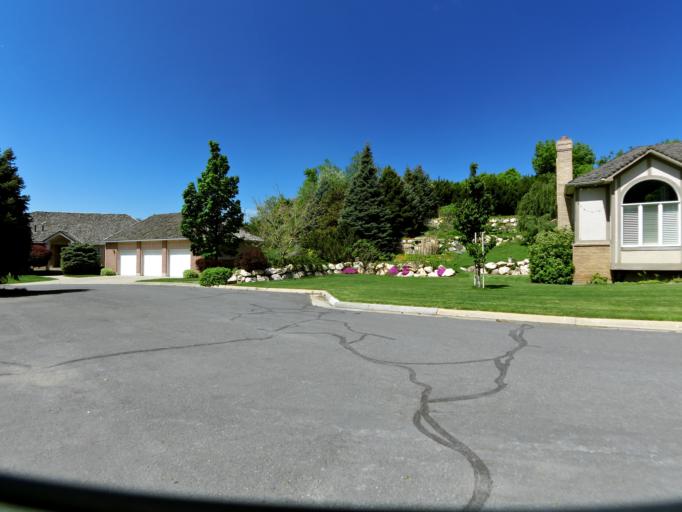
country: US
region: Utah
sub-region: Weber County
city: Uintah
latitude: 41.1758
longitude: -111.9346
